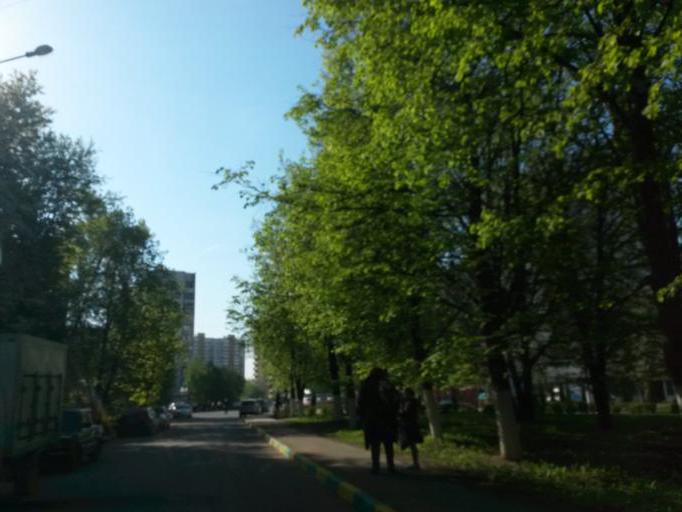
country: RU
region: Moskovskaya
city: Razvilka
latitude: 55.5897
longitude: 37.7526
